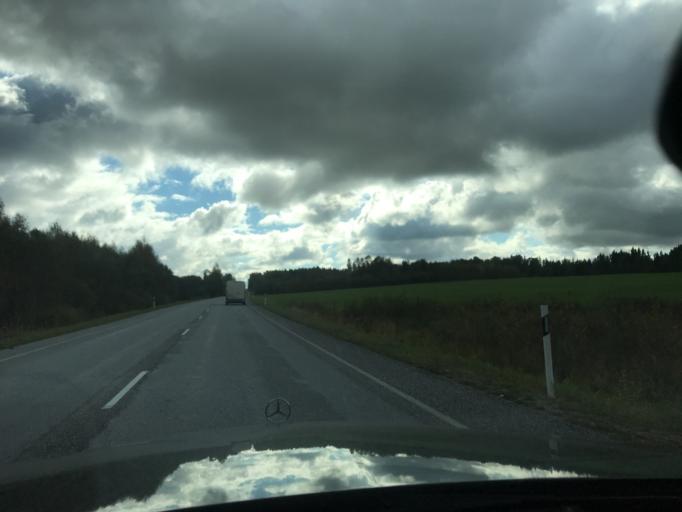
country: RU
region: Pskov
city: Pechory
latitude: 57.7200
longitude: 27.3170
